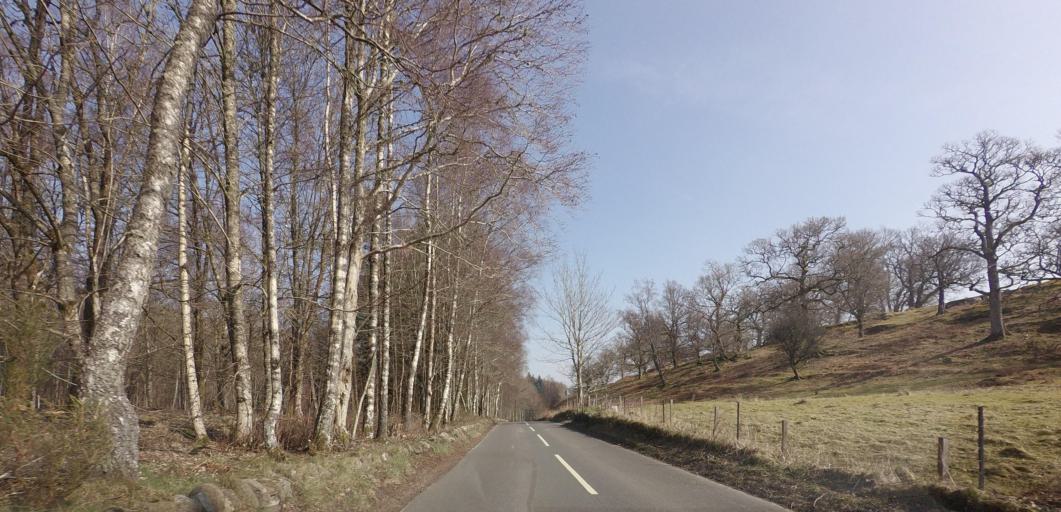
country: GB
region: Scotland
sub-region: Stirling
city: Callander
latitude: 56.4824
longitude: -4.3090
